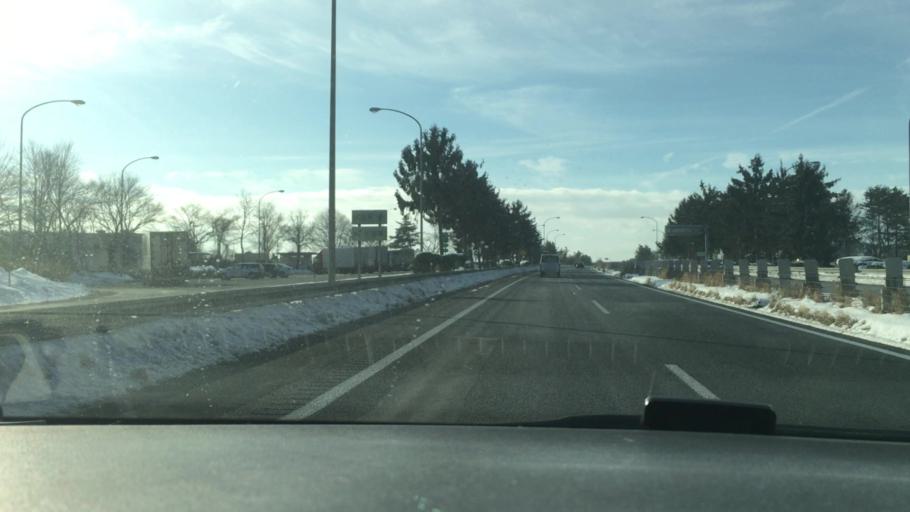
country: JP
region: Iwate
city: Hanamaki
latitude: 39.3704
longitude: 141.0927
